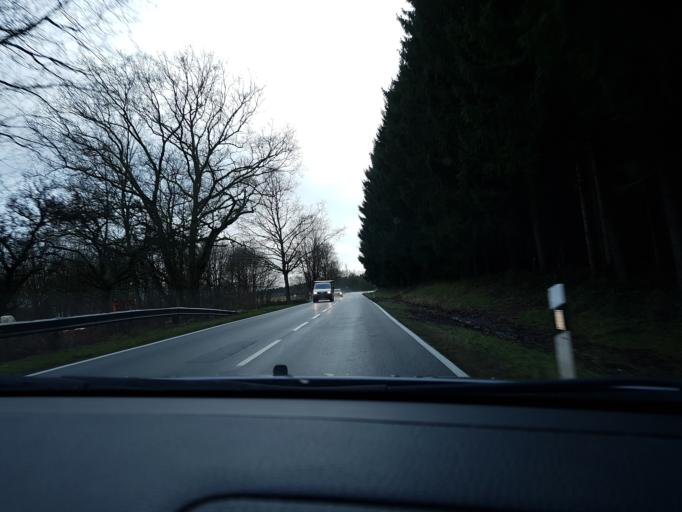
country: DE
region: Rheinland-Pfalz
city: Oberelbert
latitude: 50.3876
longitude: 7.8107
